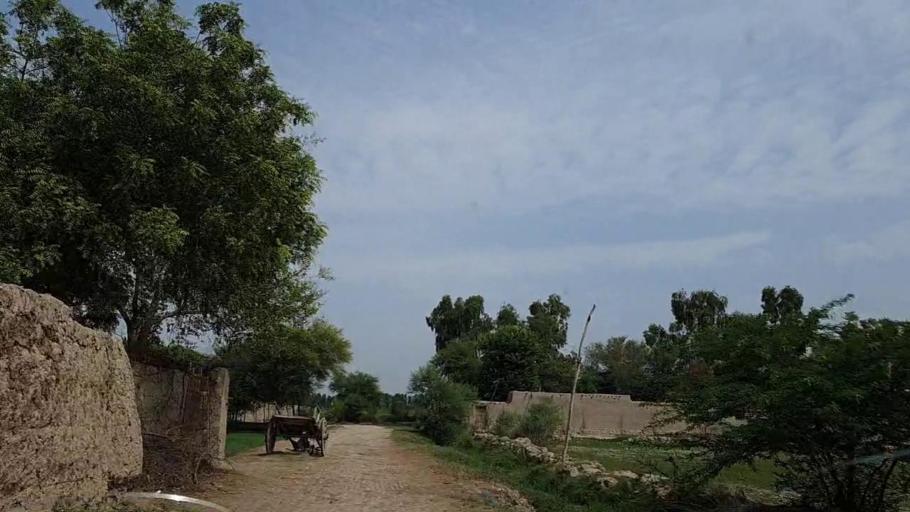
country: PK
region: Sindh
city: Khanpur
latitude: 27.8574
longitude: 69.4256
